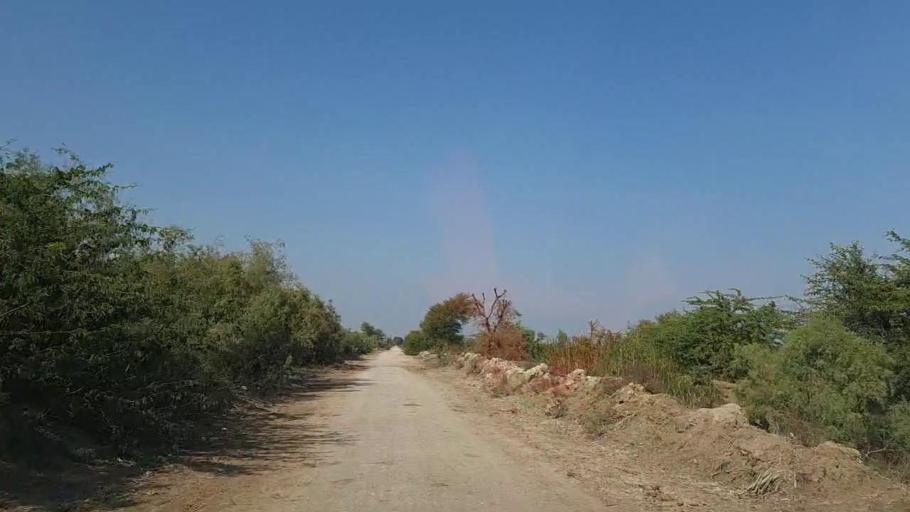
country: PK
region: Sindh
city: Sanghar
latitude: 26.0075
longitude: 69.0549
